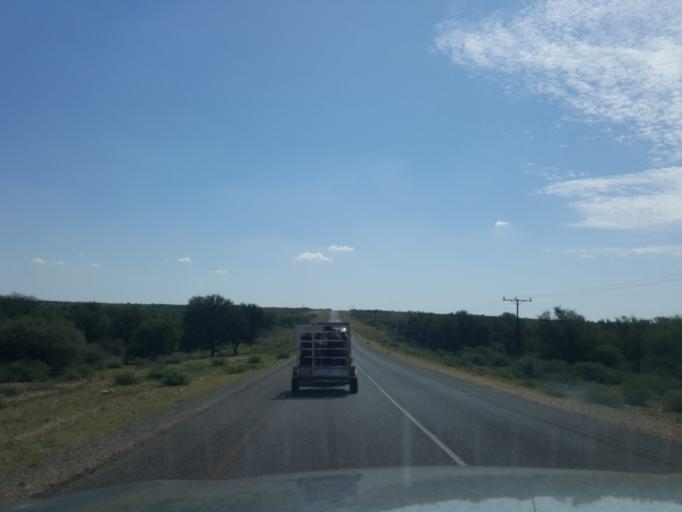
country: BW
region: Kweneng
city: Letlhakeng
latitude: -24.1187
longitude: 25.0591
